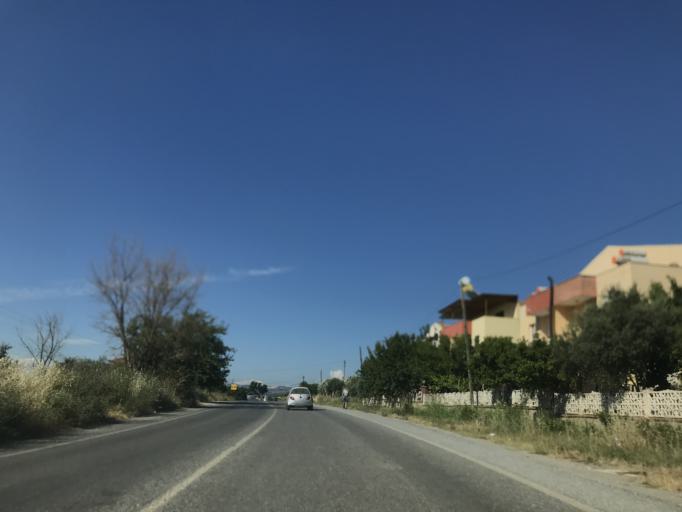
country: TR
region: Aydin
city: Davutlar
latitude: 37.7224
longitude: 27.2553
